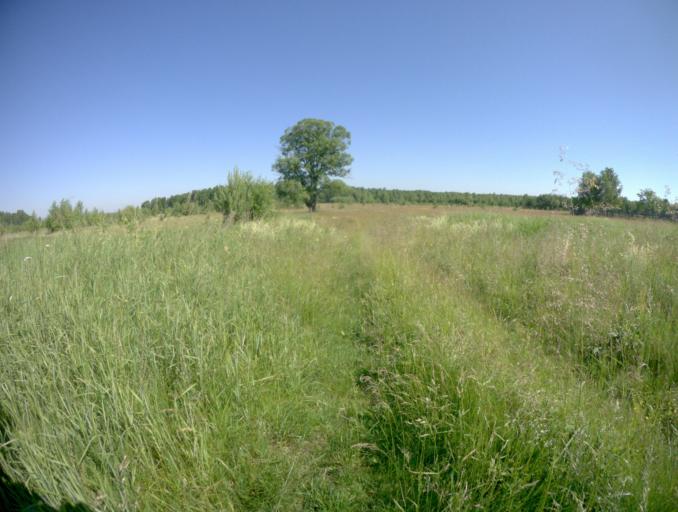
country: RU
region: Vladimir
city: Vyazniki
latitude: 56.2938
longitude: 42.3183
